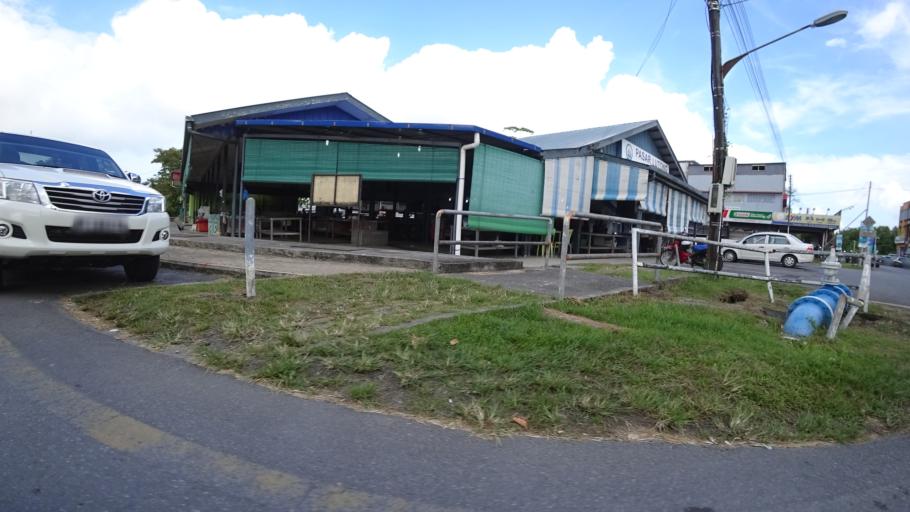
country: MY
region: Sarawak
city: Miri
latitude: 4.4673
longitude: 114.0081
